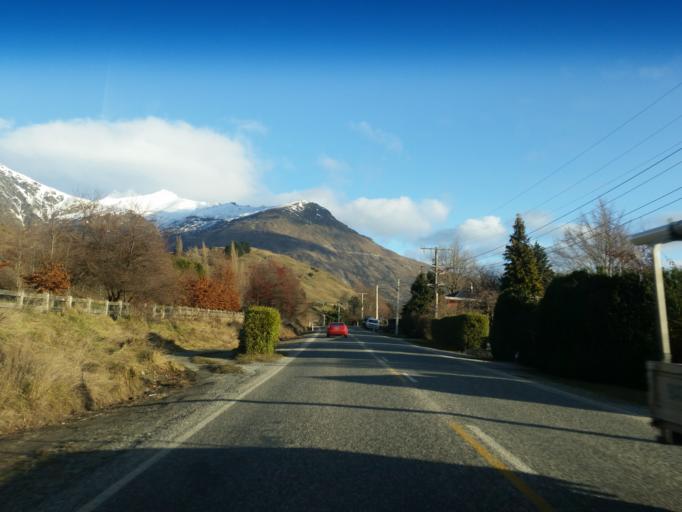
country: NZ
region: Otago
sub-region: Queenstown-Lakes District
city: Arrowtown
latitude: -44.9826
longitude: 168.8167
